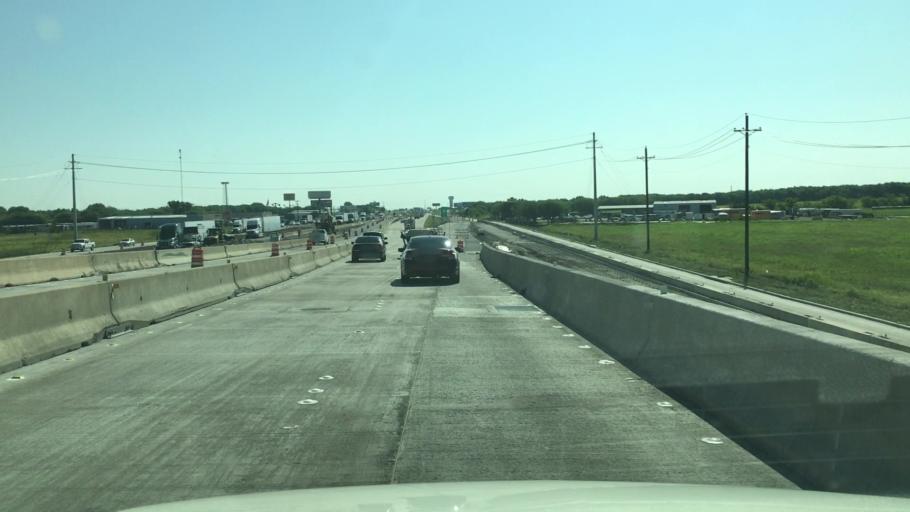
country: US
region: Texas
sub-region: Rockwall County
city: Fate
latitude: 32.9200
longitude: -96.4162
